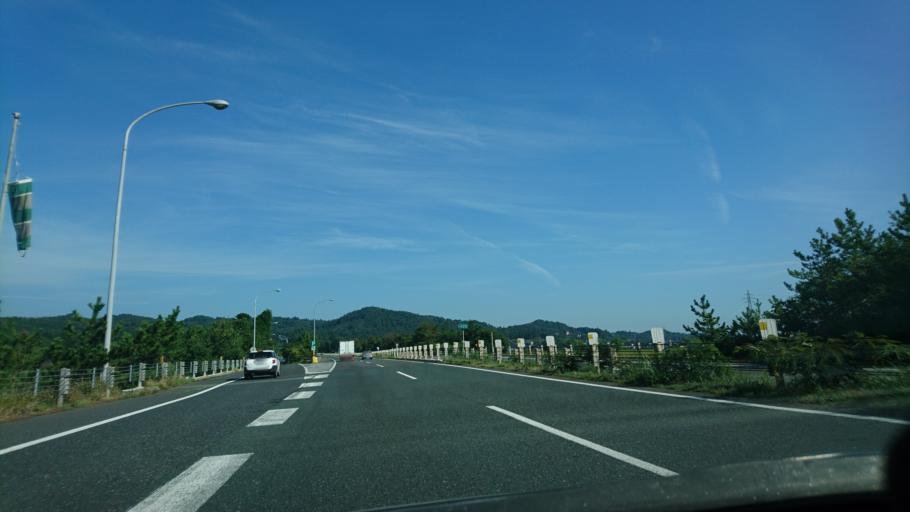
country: JP
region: Iwate
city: Ichinoseki
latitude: 38.9790
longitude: 141.1098
